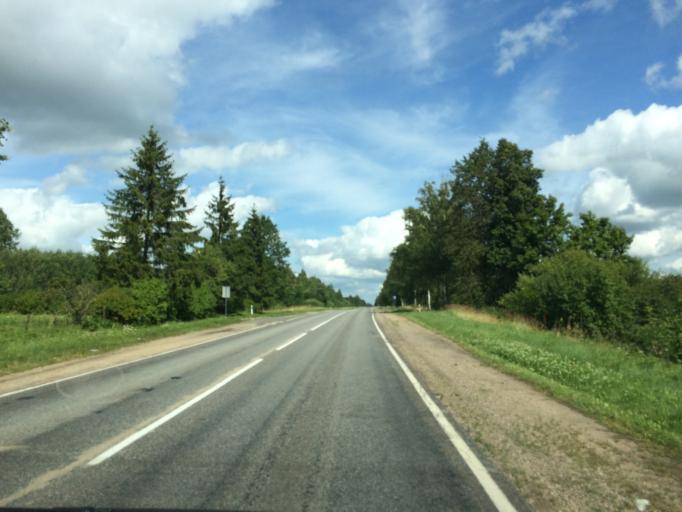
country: LV
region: Rezekne
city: Rezekne
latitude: 56.6294
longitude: 27.4641
